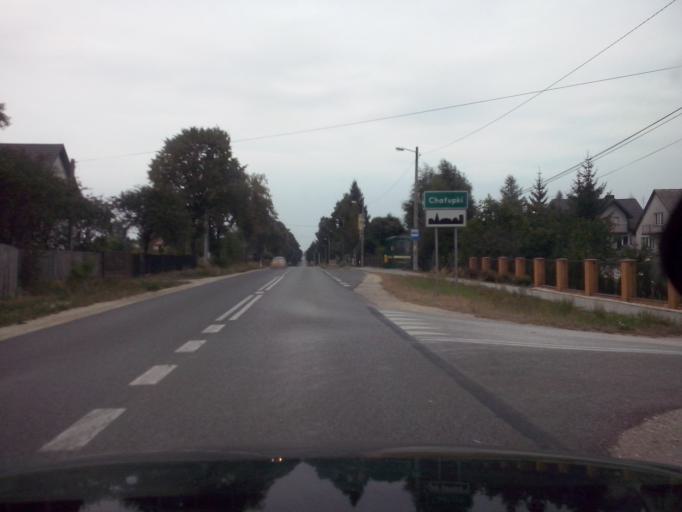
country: PL
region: Swietokrzyskie
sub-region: Powiat kielecki
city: Morawica
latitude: 50.6993
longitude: 20.6004
